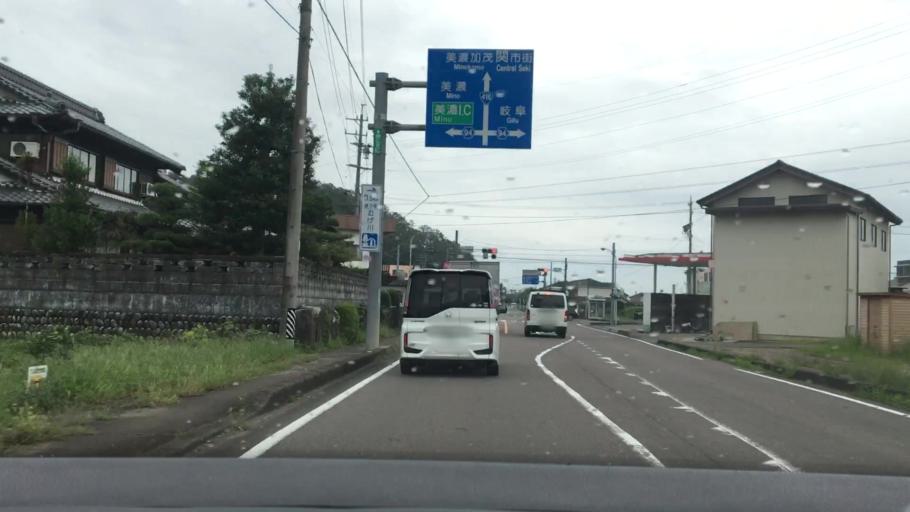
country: JP
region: Gifu
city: Mino
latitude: 35.5205
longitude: 136.8551
